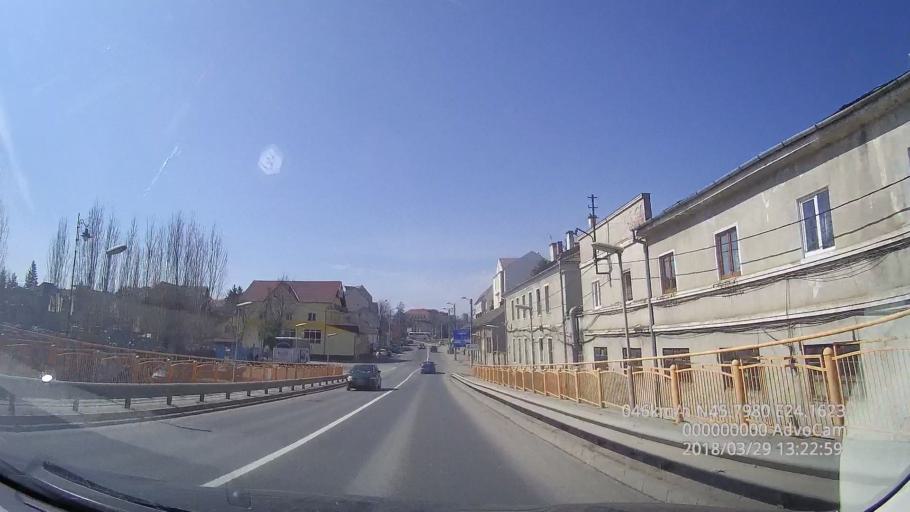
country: RO
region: Sibiu
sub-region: Municipiul Sibiu
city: Sibiu
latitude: 45.7979
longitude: 24.1621
